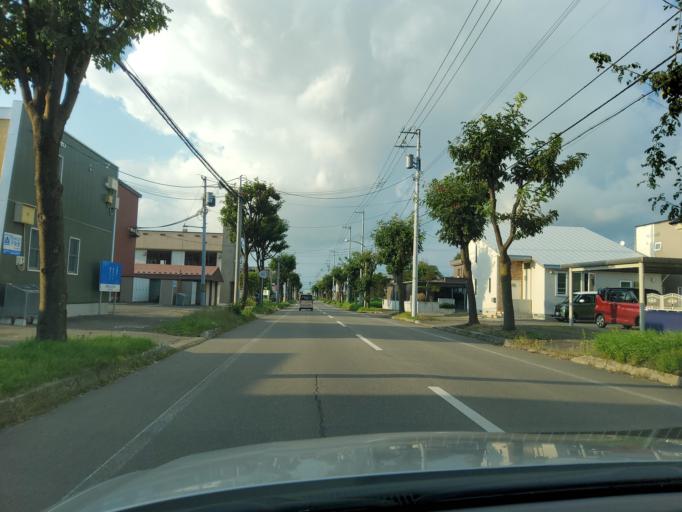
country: JP
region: Hokkaido
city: Obihiro
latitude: 42.9168
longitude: 143.1851
